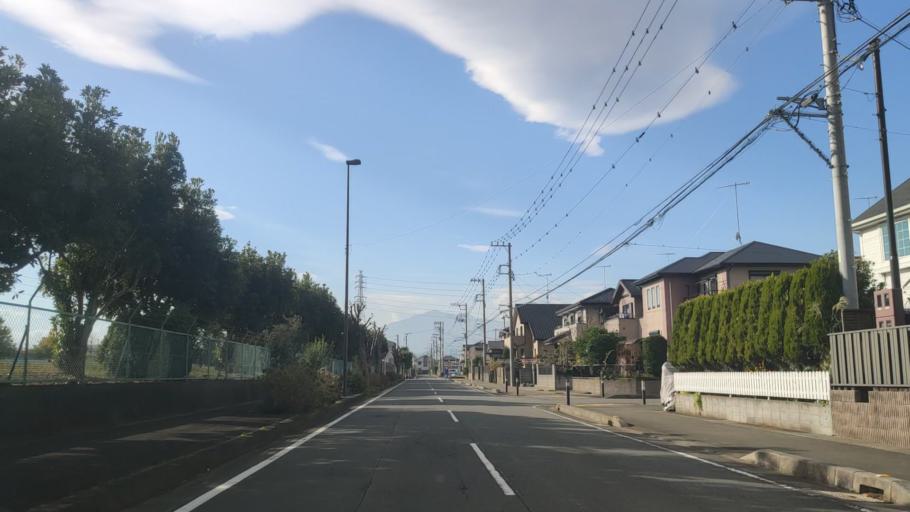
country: JP
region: Kanagawa
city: Atsugi
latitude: 35.4353
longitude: 139.3887
